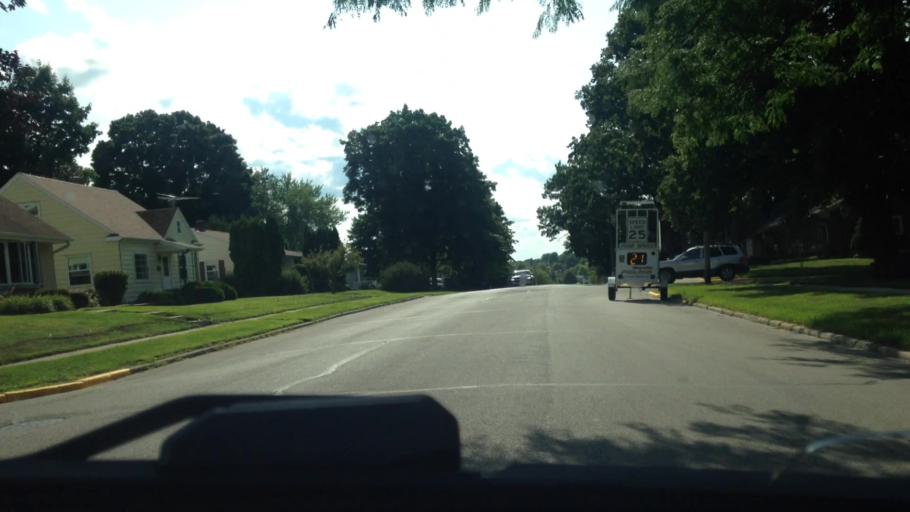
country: US
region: Wisconsin
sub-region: Dodge County
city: Mayville
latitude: 43.4976
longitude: -88.5544
